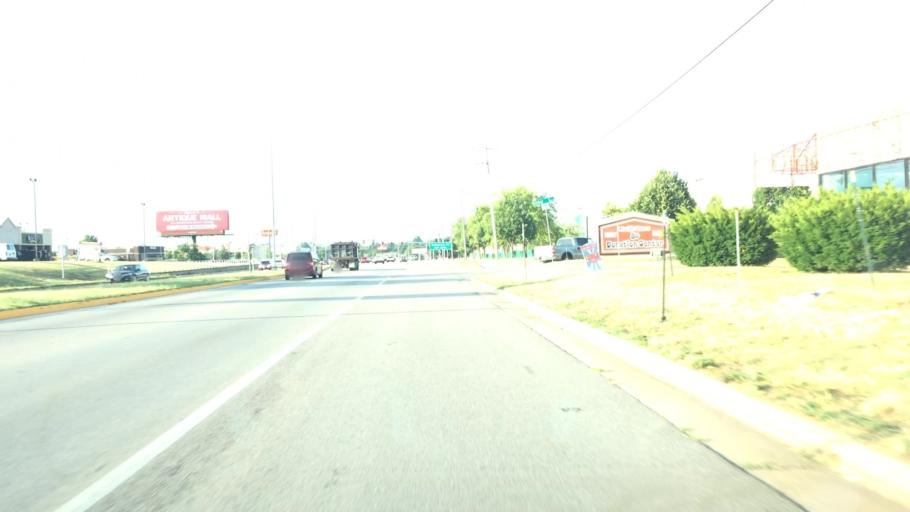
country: US
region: Missouri
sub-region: Greene County
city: Springfield
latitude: 37.1627
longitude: -93.3164
